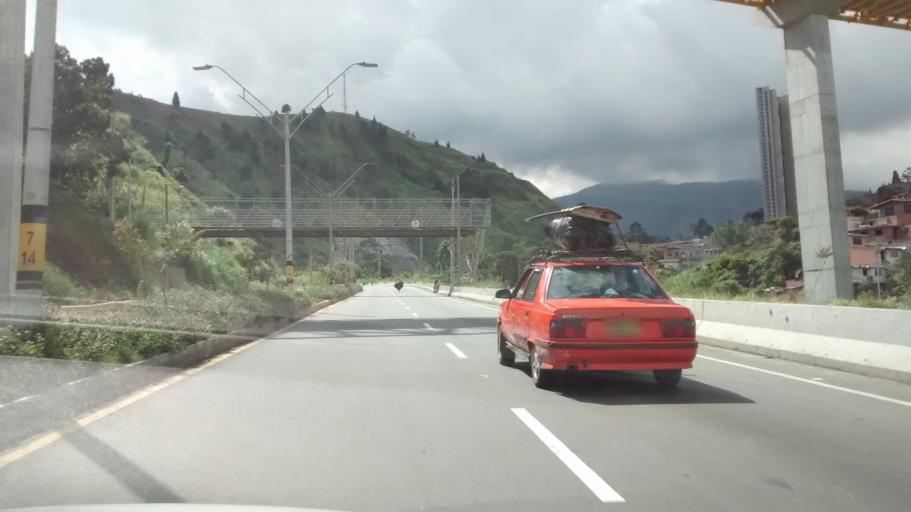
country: CO
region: Antioquia
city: Medellin
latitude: 6.2738
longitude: -75.6141
